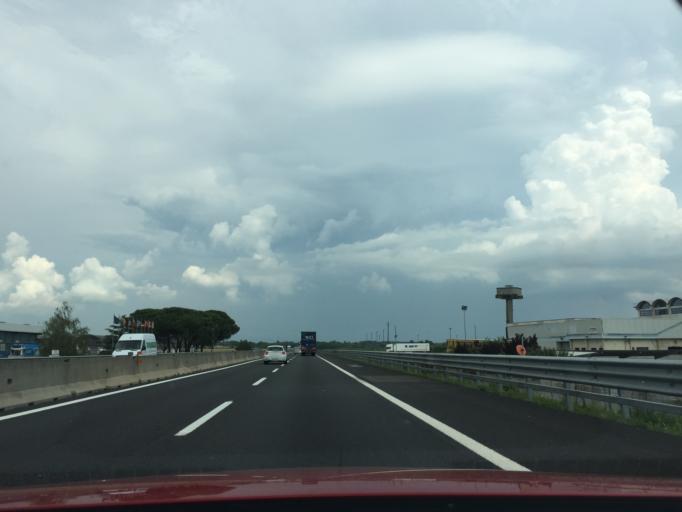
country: IT
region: Tuscany
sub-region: Provincia di Lucca
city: Porcari
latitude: 43.8194
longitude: 10.6247
